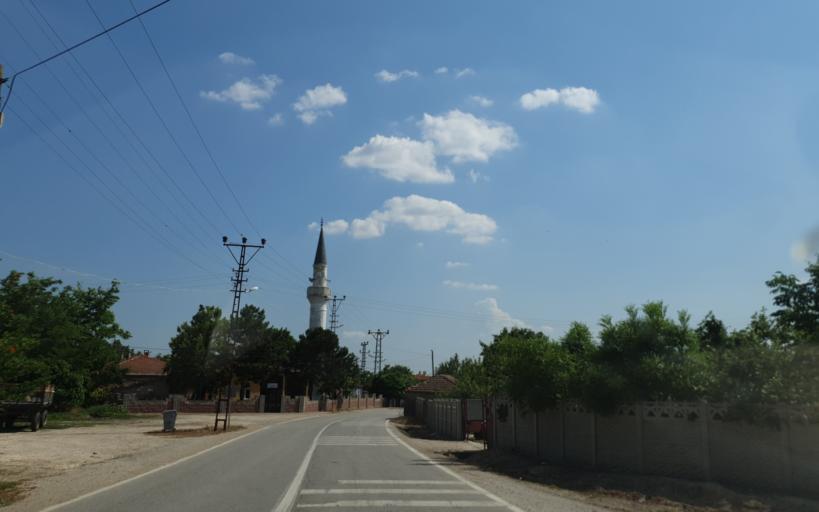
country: TR
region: Kirklareli
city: Buyukkaristiran
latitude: 41.3361
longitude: 27.5438
